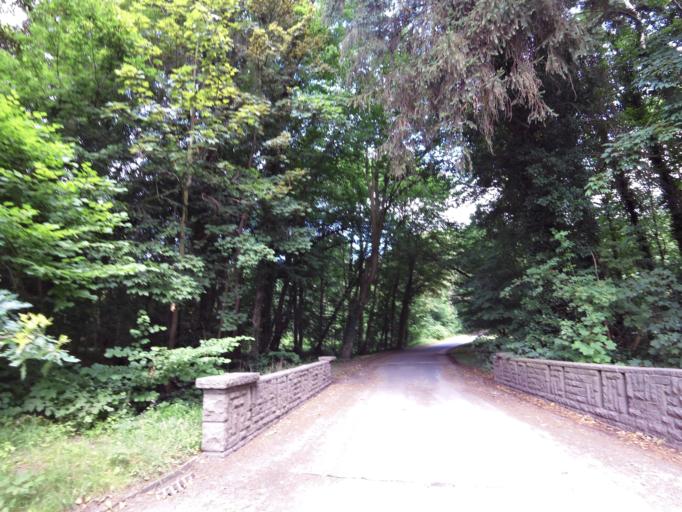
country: BE
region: Flanders
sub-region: Provincie Vlaams-Brabant
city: Bever
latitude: 50.9260
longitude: 4.3215
